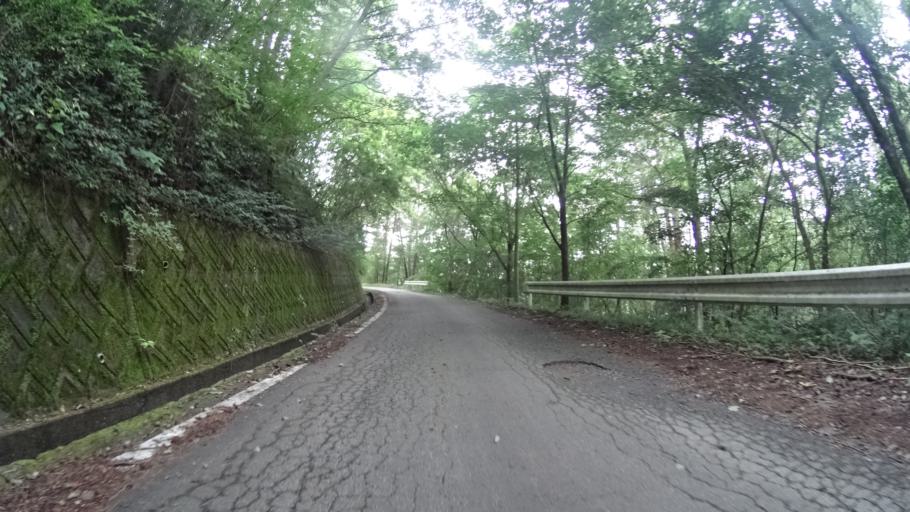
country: JP
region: Yamanashi
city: Kofu-shi
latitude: 35.8055
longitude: 138.5885
